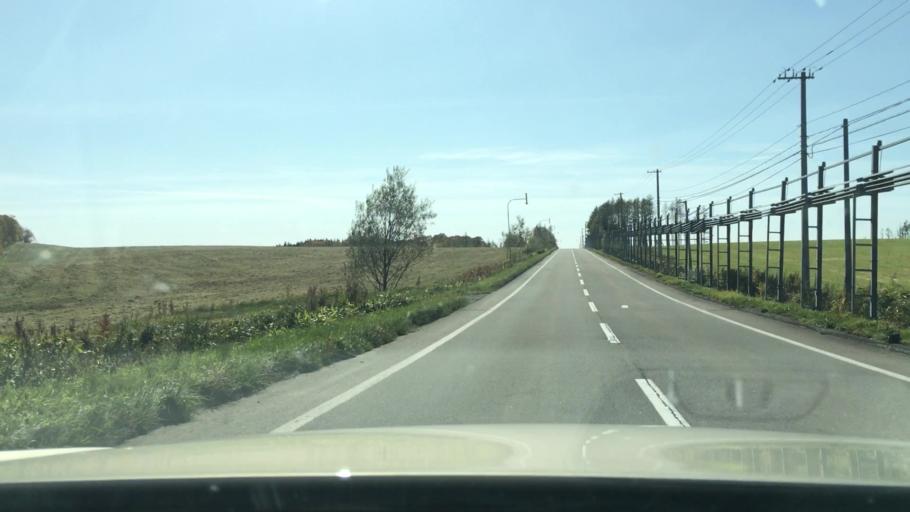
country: JP
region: Hokkaido
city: Kitami
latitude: 43.6015
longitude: 143.6832
